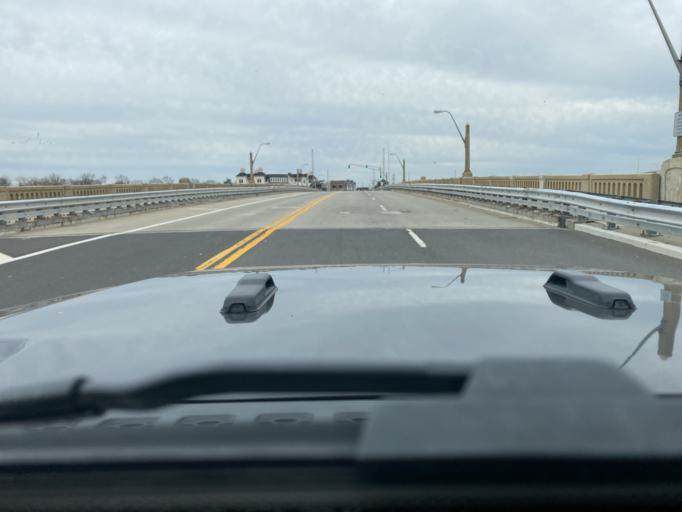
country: US
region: New Jersey
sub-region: Monmouth County
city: Avon-by-the-Sea
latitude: 40.1873
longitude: -74.0233
